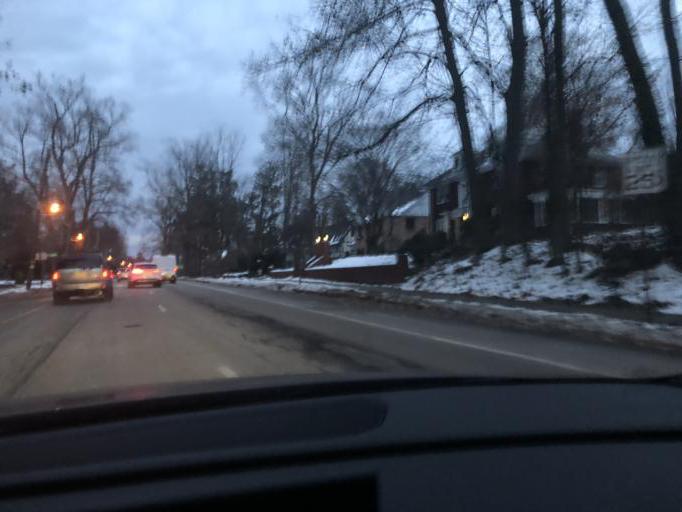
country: US
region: New Jersey
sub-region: Morris County
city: Morristown
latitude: 40.7961
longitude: -74.4653
